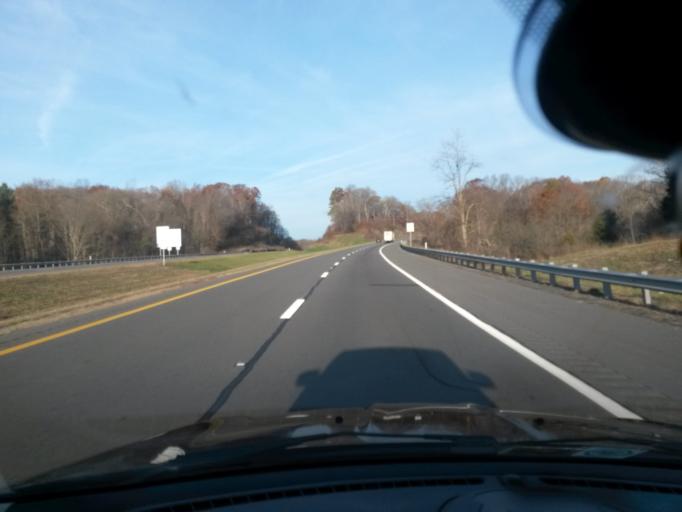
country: US
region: West Virginia
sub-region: Greenbrier County
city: Lewisburg
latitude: 37.8209
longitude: -80.4388
